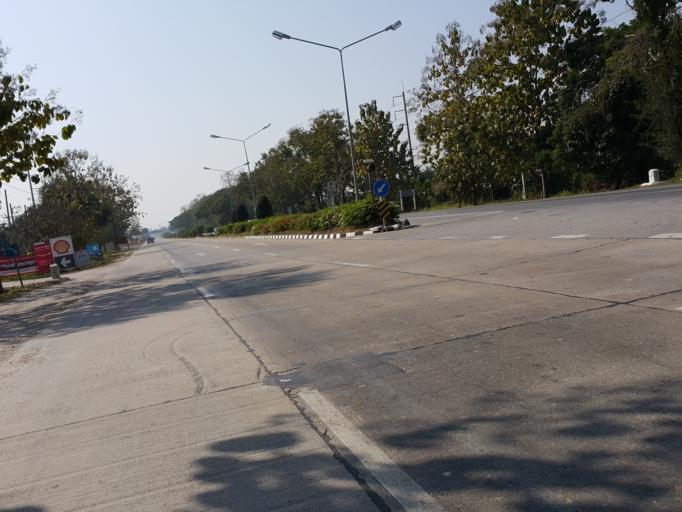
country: TH
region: Lamphun
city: Lamphun
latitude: 18.6235
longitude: 99.0480
